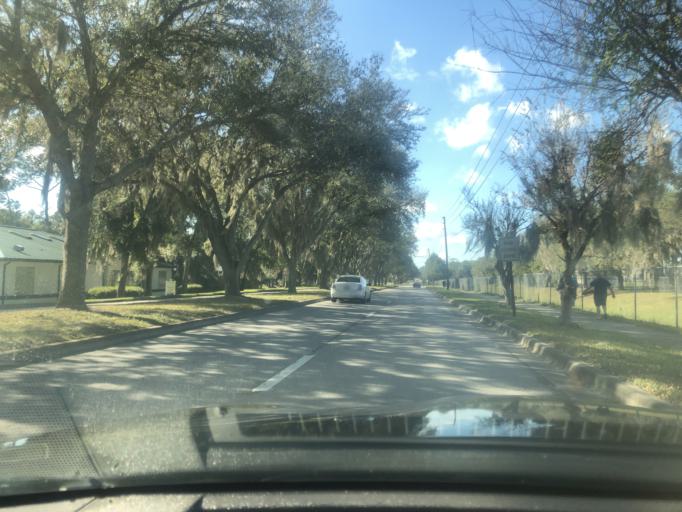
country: US
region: Florida
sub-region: Citrus County
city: Inverness
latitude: 28.8323
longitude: -82.3394
